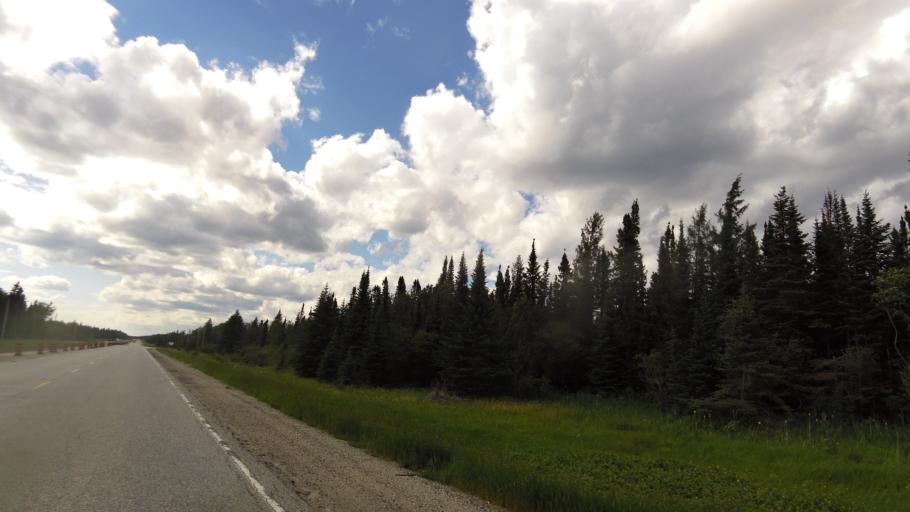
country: CA
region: Ontario
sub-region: Algoma
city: Hornepayne
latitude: 49.7512
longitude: -84.4009
